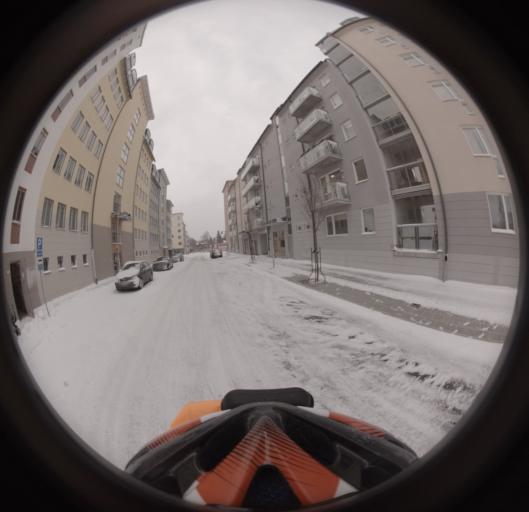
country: SE
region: Stockholm
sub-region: Sollentuna Kommun
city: Sollentuna
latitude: 59.4327
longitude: 17.9430
